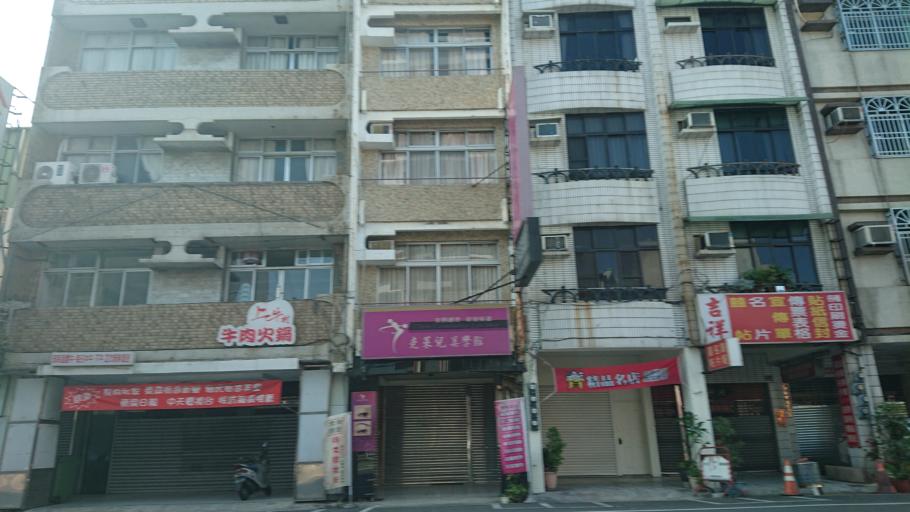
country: TW
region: Taiwan
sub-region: Tainan
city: Tainan
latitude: 22.9957
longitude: 120.1957
